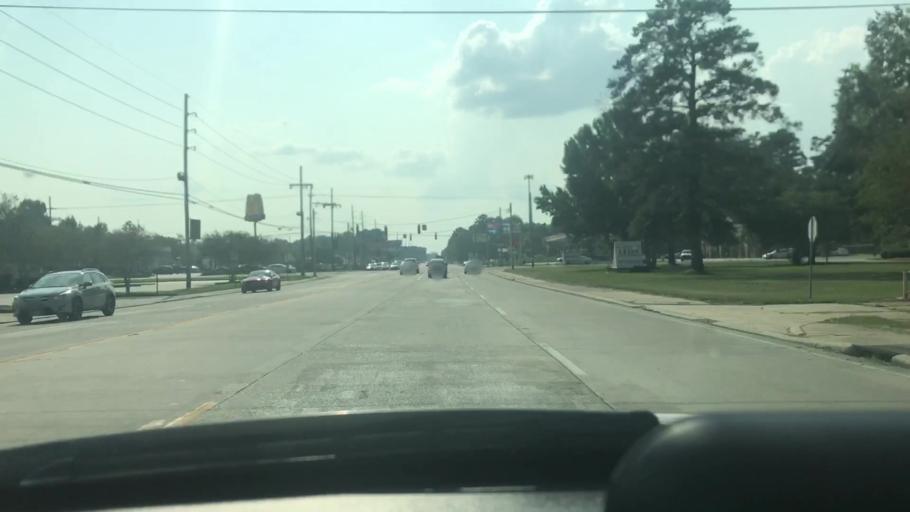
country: US
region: Louisiana
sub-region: Tangipahoa Parish
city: Hammond
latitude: 30.5192
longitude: -90.4815
